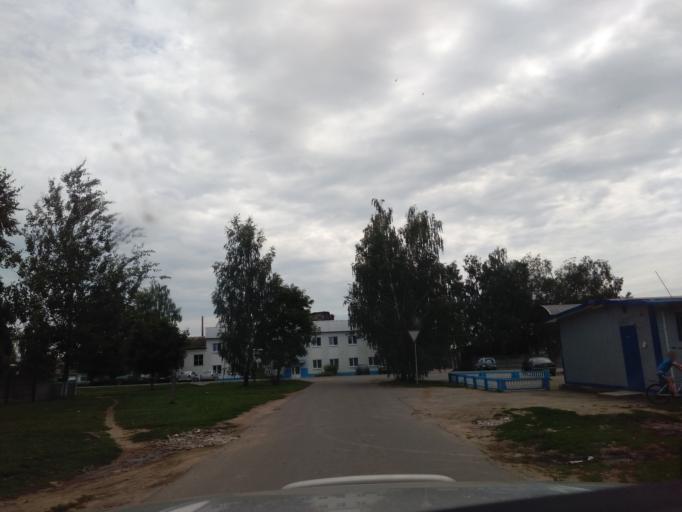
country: BY
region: Minsk
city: Kapyl'
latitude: 53.1391
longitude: 27.0947
